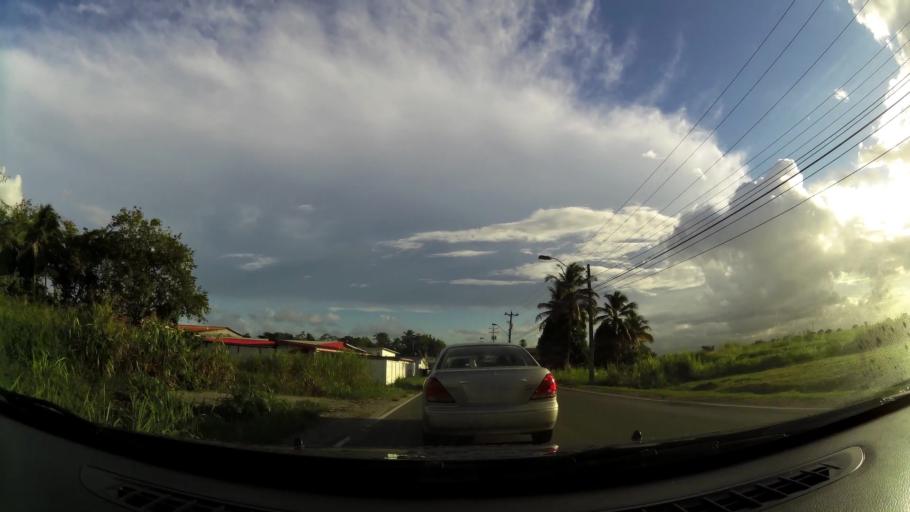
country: TT
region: Tunapuna/Piarco
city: Tunapuna
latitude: 10.5937
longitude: -61.3675
